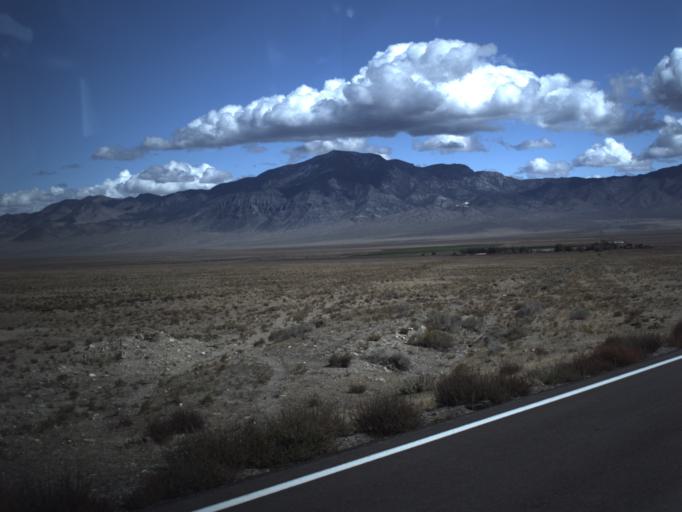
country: US
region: Utah
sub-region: Beaver County
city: Milford
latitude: 38.4858
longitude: -113.4541
